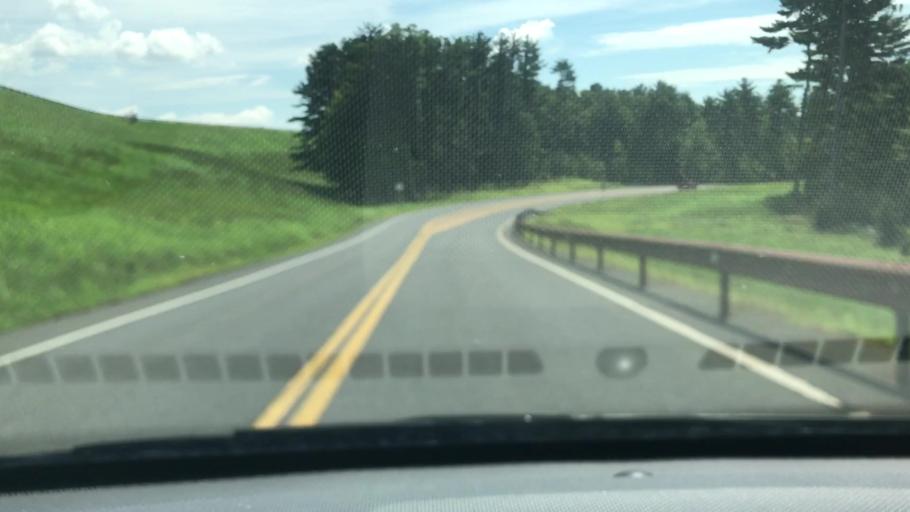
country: US
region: New York
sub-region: Ulster County
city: Shokan
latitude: 41.9499
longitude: -74.2035
